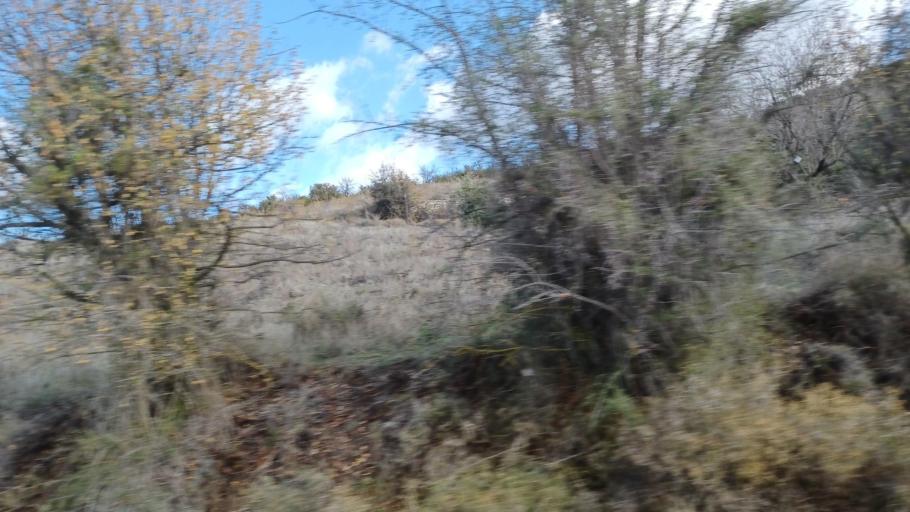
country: CY
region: Limassol
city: Pachna
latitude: 34.8586
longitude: 32.6925
